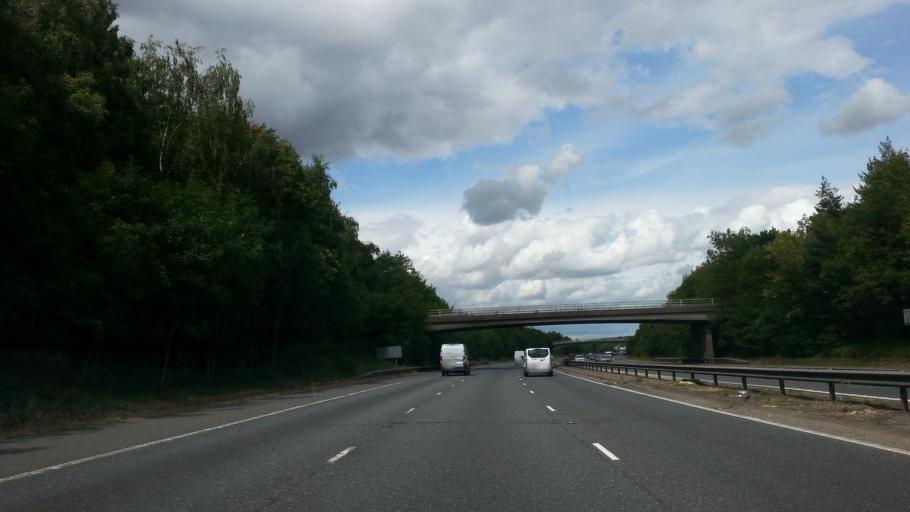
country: GB
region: England
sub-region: Essex
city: Little Hallingbury
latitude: 51.8491
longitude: 0.1848
